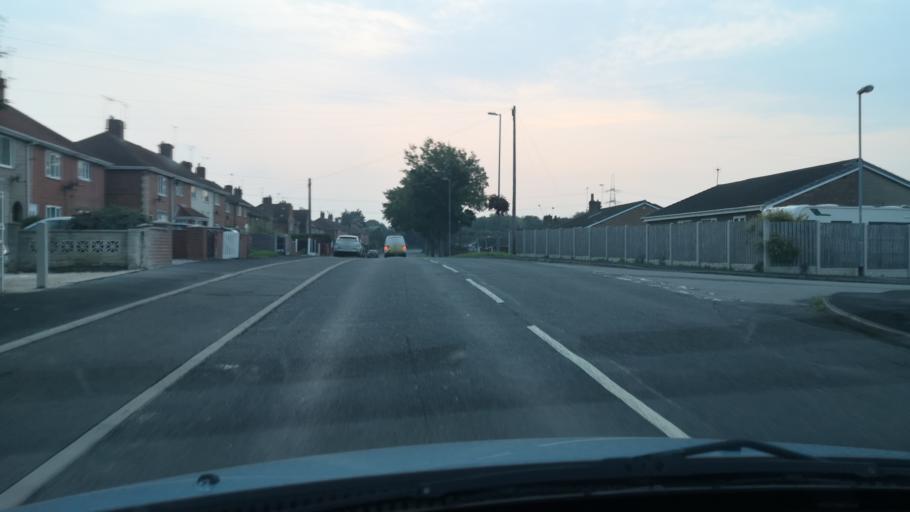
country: GB
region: England
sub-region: City and Borough of Wakefield
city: North Elmsall
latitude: 53.6159
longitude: -1.2573
